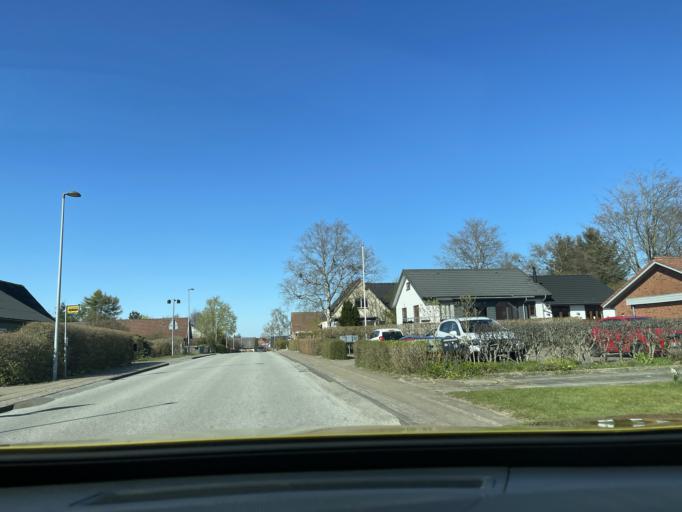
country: DK
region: Central Jutland
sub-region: Ikast-Brande Kommune
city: Bording Kirkeby
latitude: 56.1425
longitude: 9.2745
